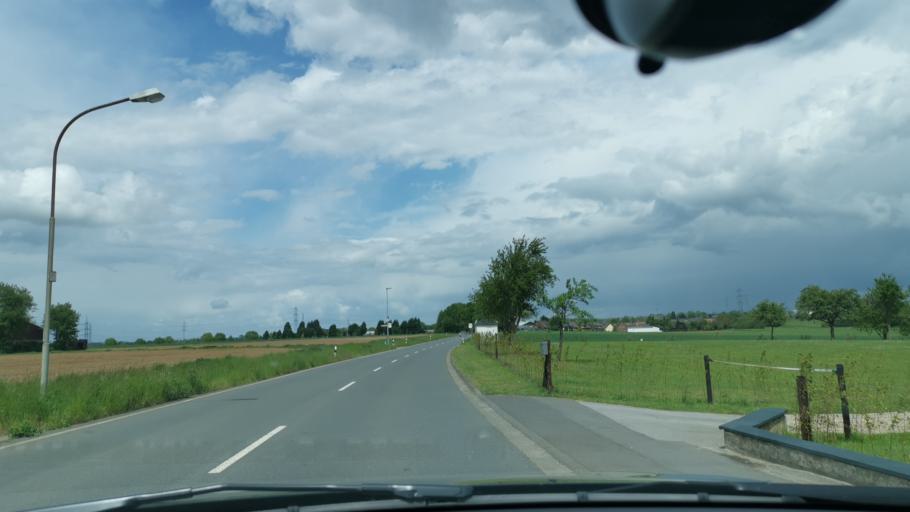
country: DE
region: North Rhine-Westphalia
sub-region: Regierungsbezirk Dusseldorf
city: Rommerskirchen
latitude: 51.0778
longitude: 6.6883
